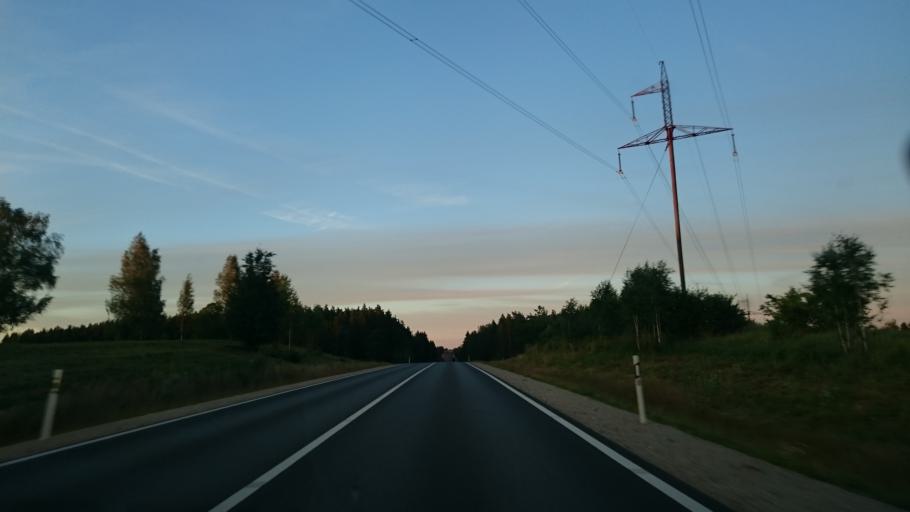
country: LV
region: Jaunpils
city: Jaunpils
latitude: 56.6821
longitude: 23.1010
